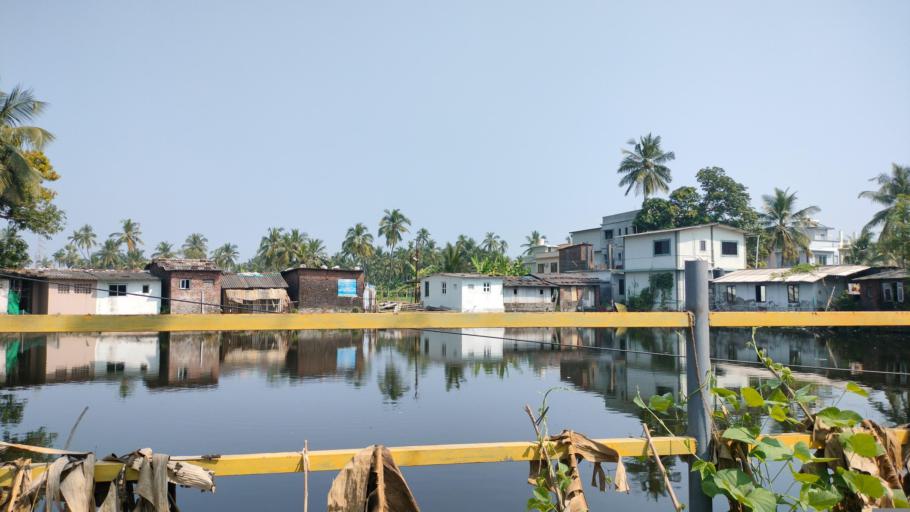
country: IN
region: Maharashtra
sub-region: Thane
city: Virar
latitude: 19.4103
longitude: 72.7844
